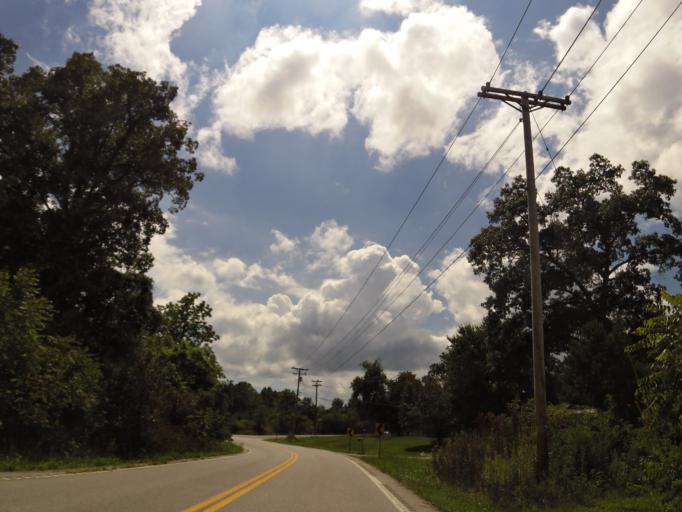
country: US
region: Tennessee
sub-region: Roane County
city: Rockwood
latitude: 35.8896
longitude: -84.7415
